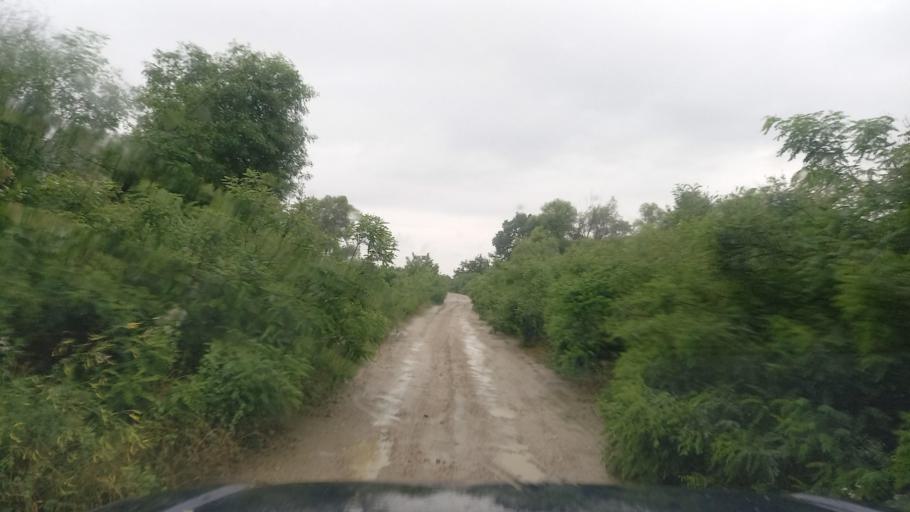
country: RU
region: Krasnodarskiy
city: Vasyurinskaya
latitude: 45.0307
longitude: 39.4750
